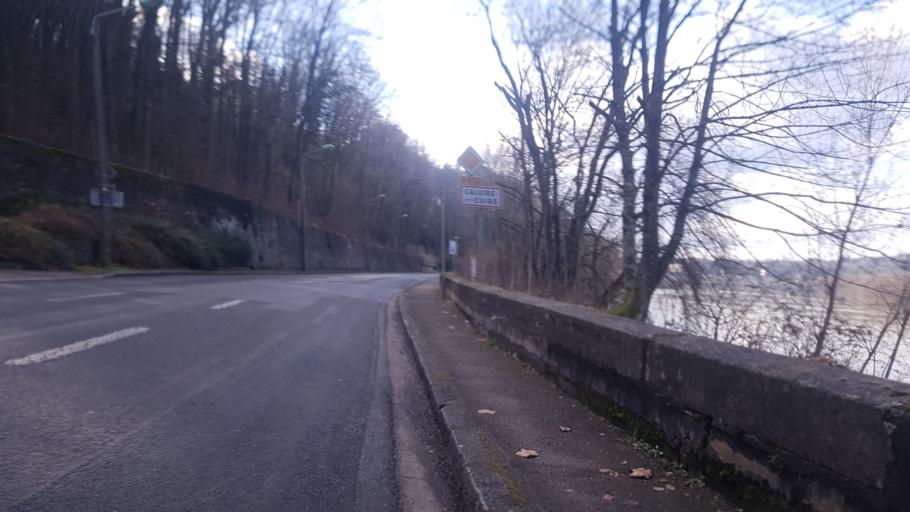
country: FR
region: Rhone-Alpes
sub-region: Departement du Rhone
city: Sathonay-Camp
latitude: 45.8180
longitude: 4.8568
